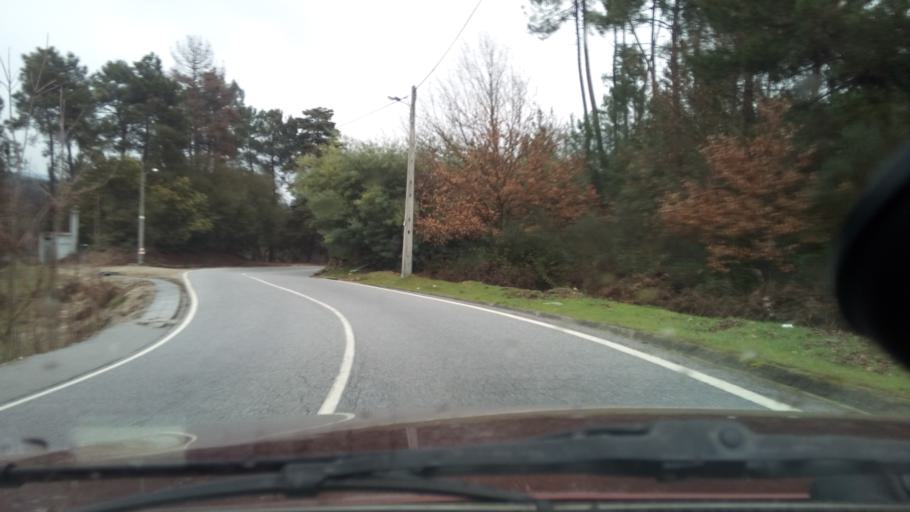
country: PT
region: Viseu
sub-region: Viseu
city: Rio de Loba
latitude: 40.6404
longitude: -7.8454
